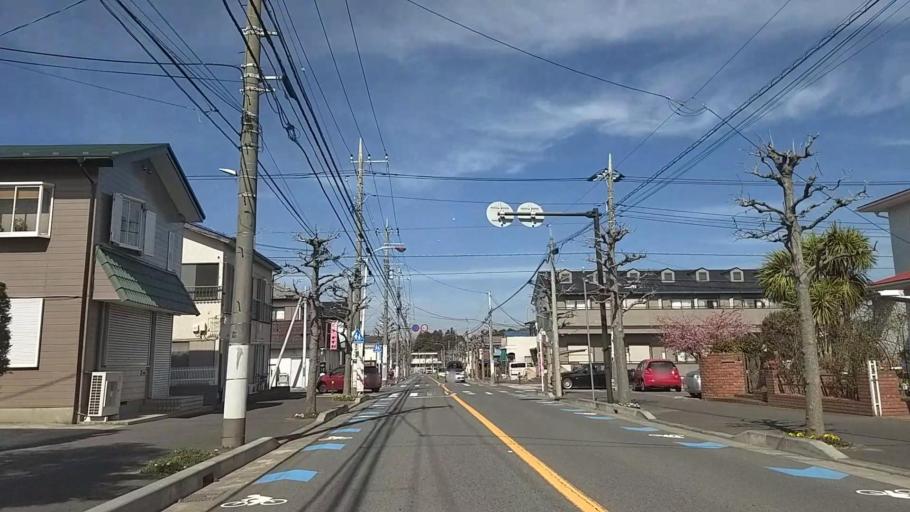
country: JP
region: Kanagawa
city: Fujisawa
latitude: 35.3998
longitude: 139.4726
